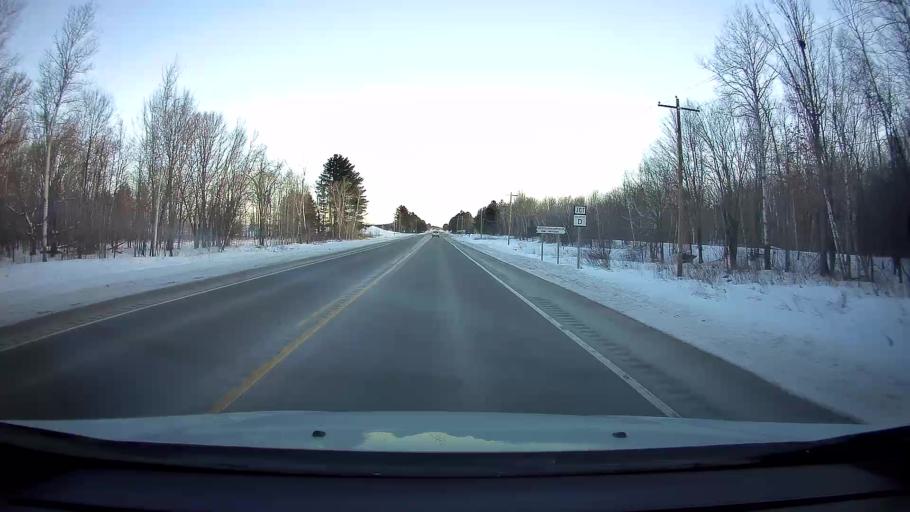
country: US
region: Wisconsin
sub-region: Washburn County
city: Shell Lake
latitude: 45.7220
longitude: -91.9368
